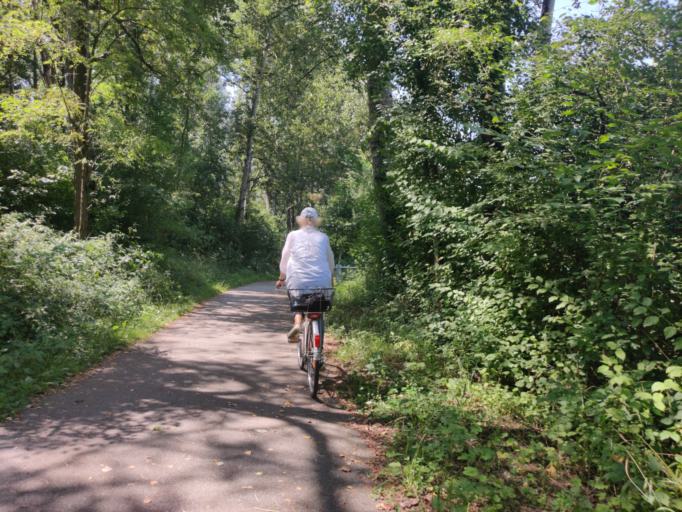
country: AT
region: Upper Austria
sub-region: Politischer Bezirk Urfahr-Umgebung
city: Ottensheim
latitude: 48.3214
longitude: 14.1444
